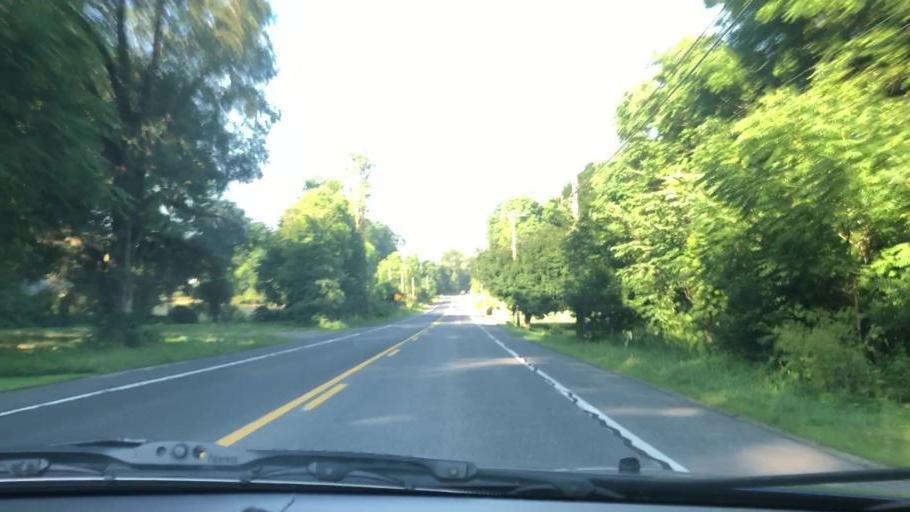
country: US
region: Pennsylvania
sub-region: Cumberland County
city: Carlisle
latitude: 40.1877
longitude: -77.2498
